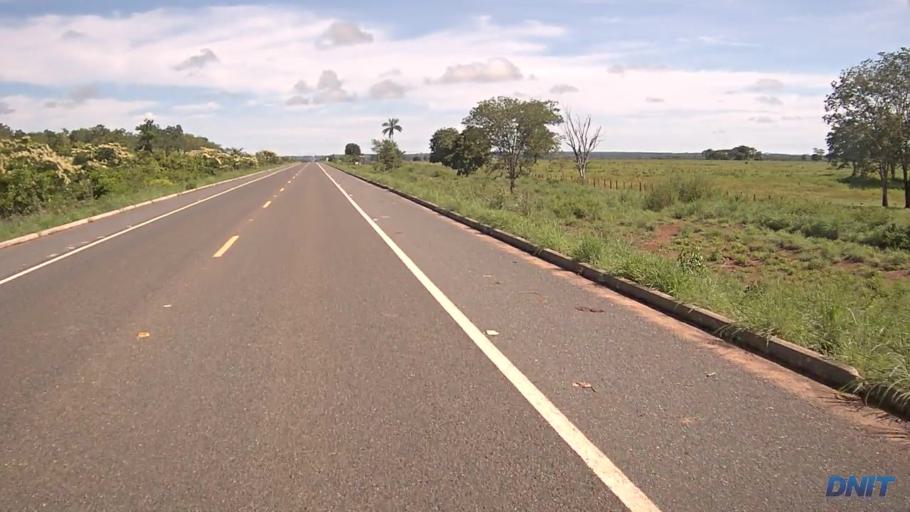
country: BR
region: Goias
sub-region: Sao Miguel Do Araguaia
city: Sao Miguel do Araguaia
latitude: -13.4153
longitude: -50.1308
